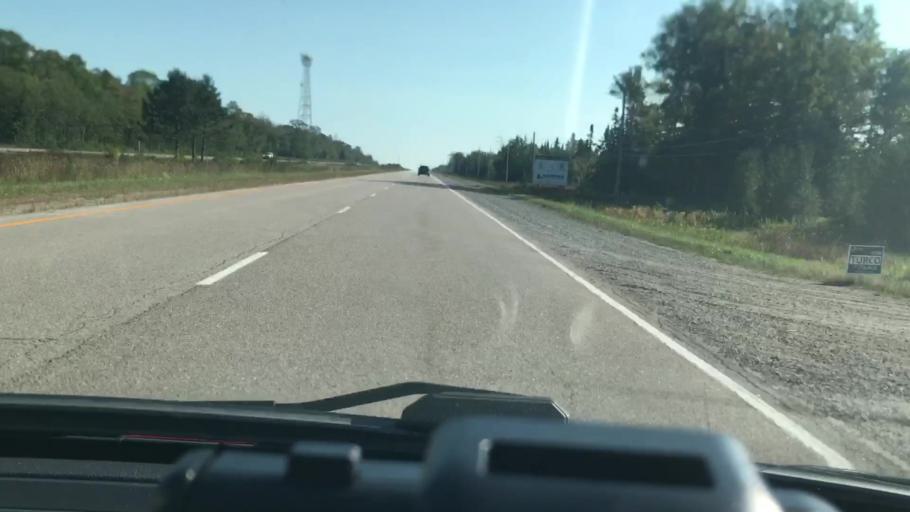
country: CA
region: Ontario
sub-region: Algoma
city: Sault Ste. Marie
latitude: 46.3930
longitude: -84.0679
